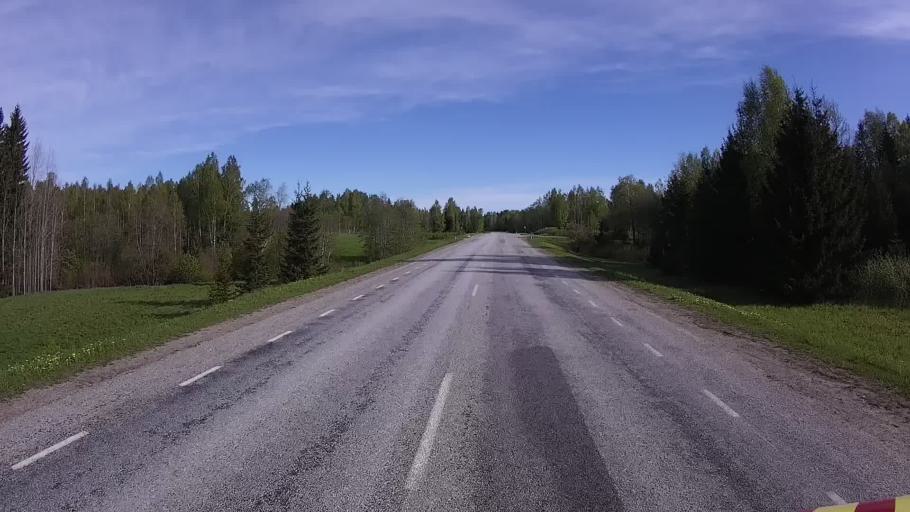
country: EE
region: Tartu
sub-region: Elva linn
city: Elva
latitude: 58.0721
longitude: 26.4987
